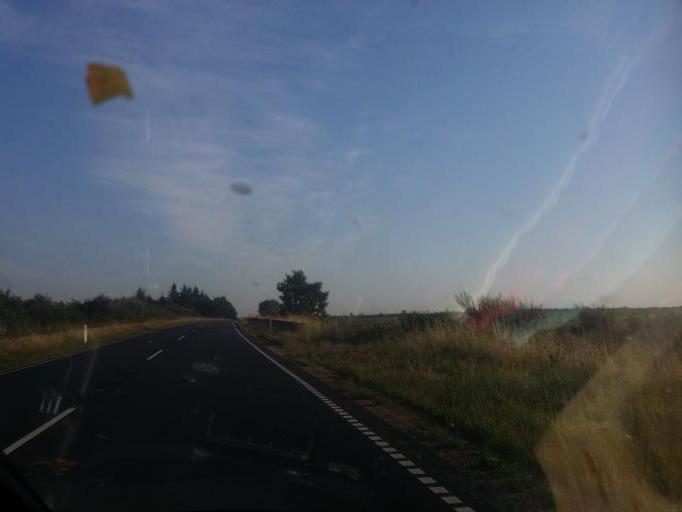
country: DK
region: South Denmark
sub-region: Tonder Kommune
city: Tonder
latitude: 54.9403
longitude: 8.8882
